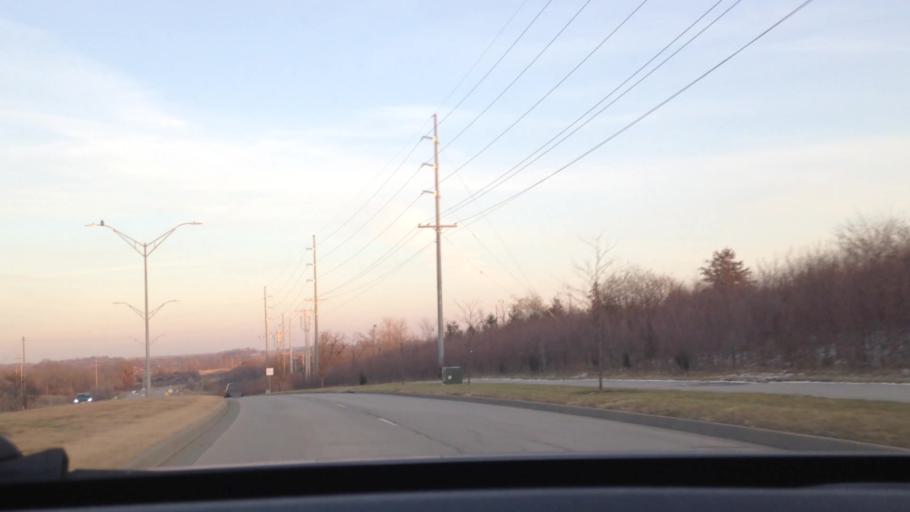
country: US
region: Missouri
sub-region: Clay County
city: Pleasant Valley
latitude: 39.2090
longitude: -94.4641
